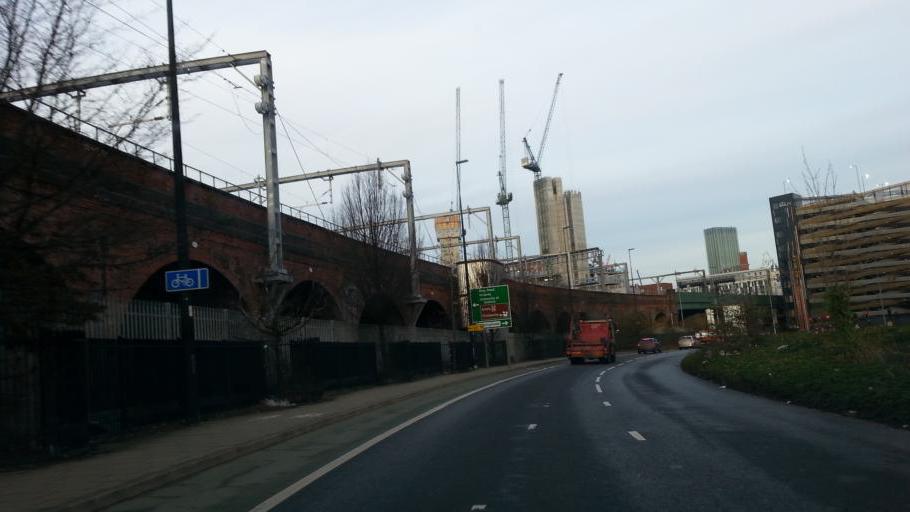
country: GB
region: England
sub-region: Manchester
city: Hulme
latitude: 53.4806
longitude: -2.2584
